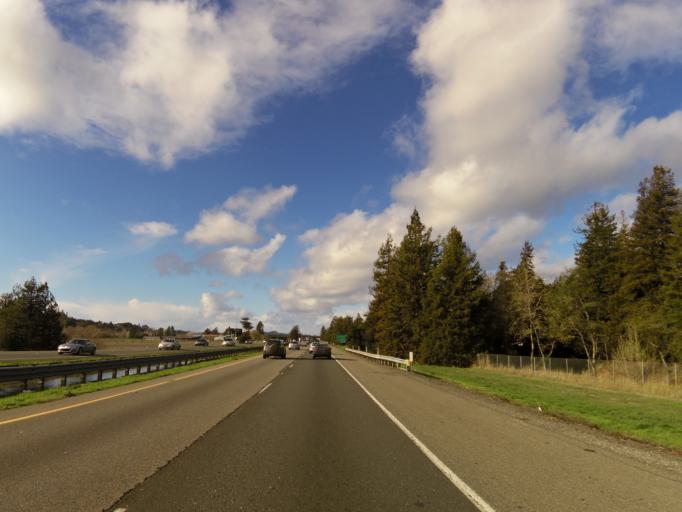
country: US
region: California
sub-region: Sonoma County
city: Petaluma
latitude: 38.2600
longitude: -122.6521
